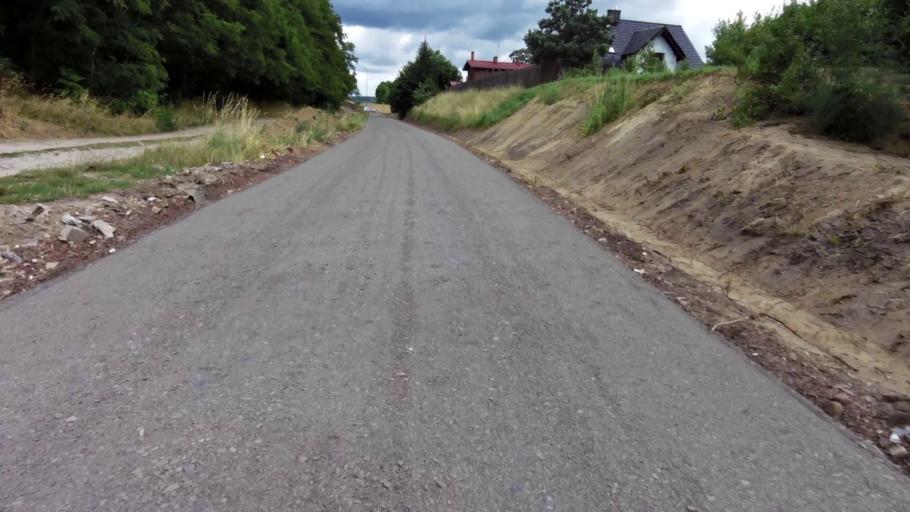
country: PL
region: West Pomeranian Voivodeship
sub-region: Powiat mysliborski
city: Barlinek
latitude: 52.9902
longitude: 15.2076
